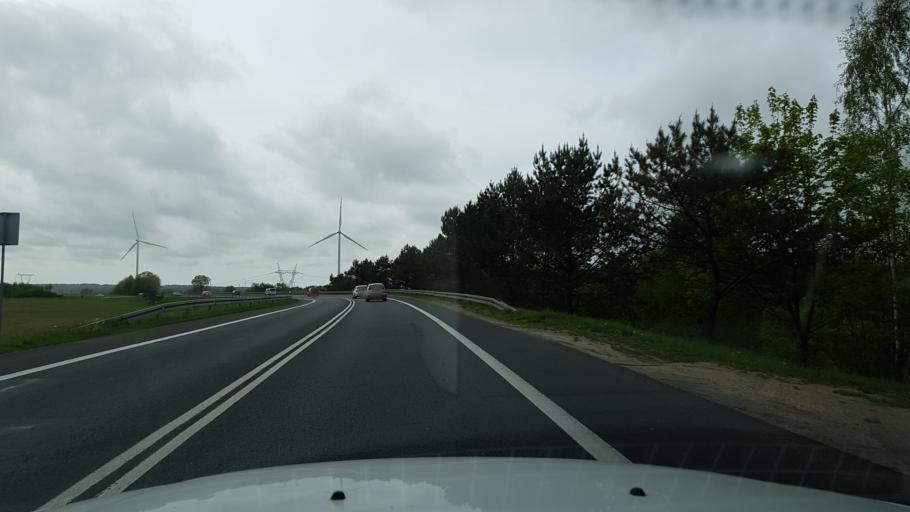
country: PL
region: West Pomeranian Voivodeship
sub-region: Powiat slawienski
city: Darlowo
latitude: 54.2774
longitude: 16.4439
